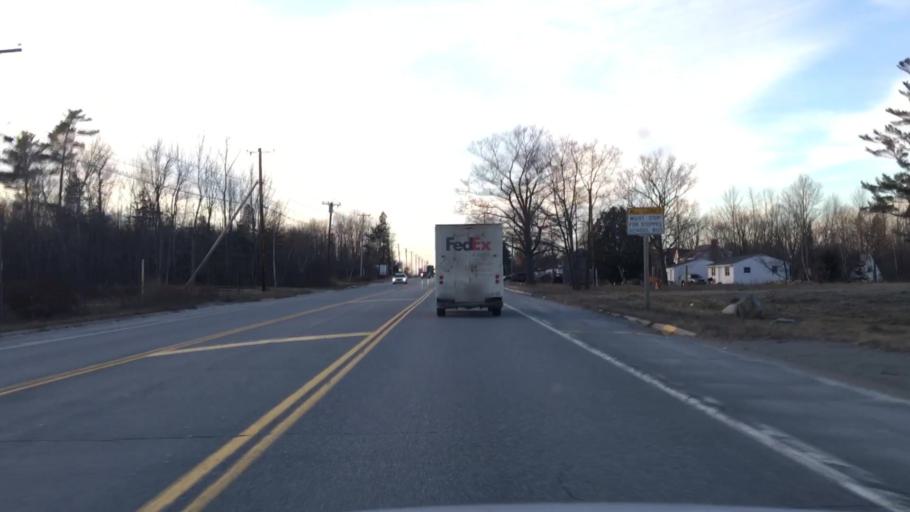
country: US
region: Maine
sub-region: Penobscot County
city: Holden
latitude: 44.7620
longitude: -68.6995
